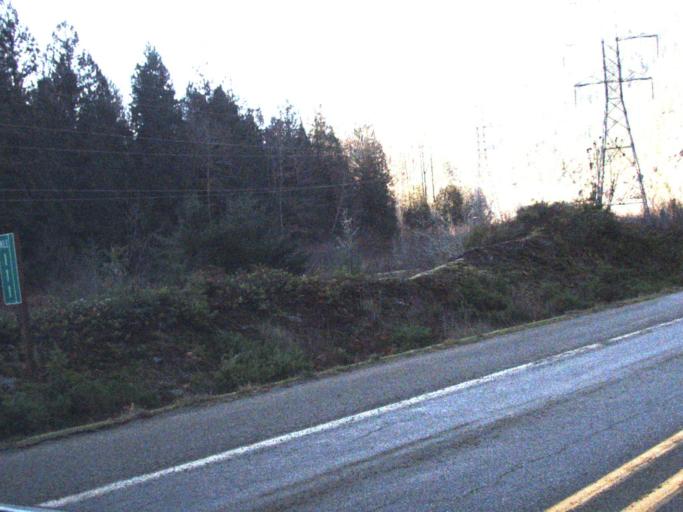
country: US
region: Washington
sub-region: Snohomish County
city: Darrington
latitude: 48.5884
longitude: -121.3911
